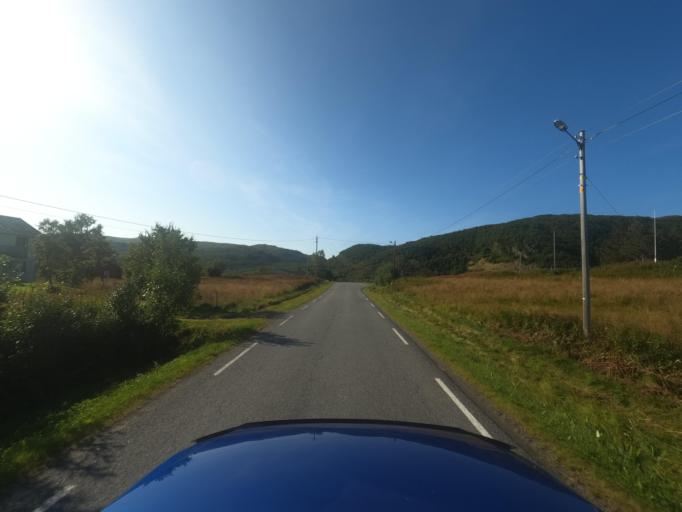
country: NO
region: Nordland
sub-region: Vestvagoy
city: Evjen
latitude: 68.2993
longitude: 13.8701
